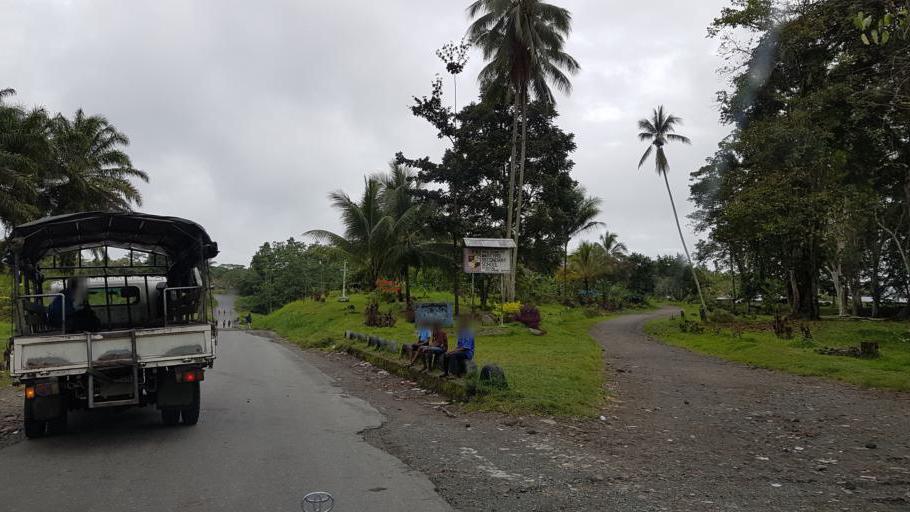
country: PG
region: Northern Province
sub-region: Sohe
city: Popondetta
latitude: -8.8200
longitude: 148.1036
